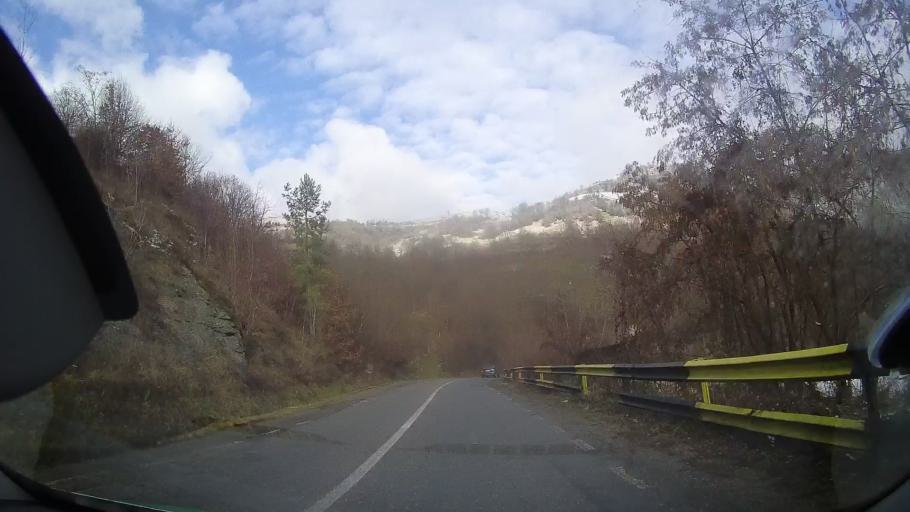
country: RO
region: Alba
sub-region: Comuna Lupsa
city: Lupsa
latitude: 46.3827
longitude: 23.2302
